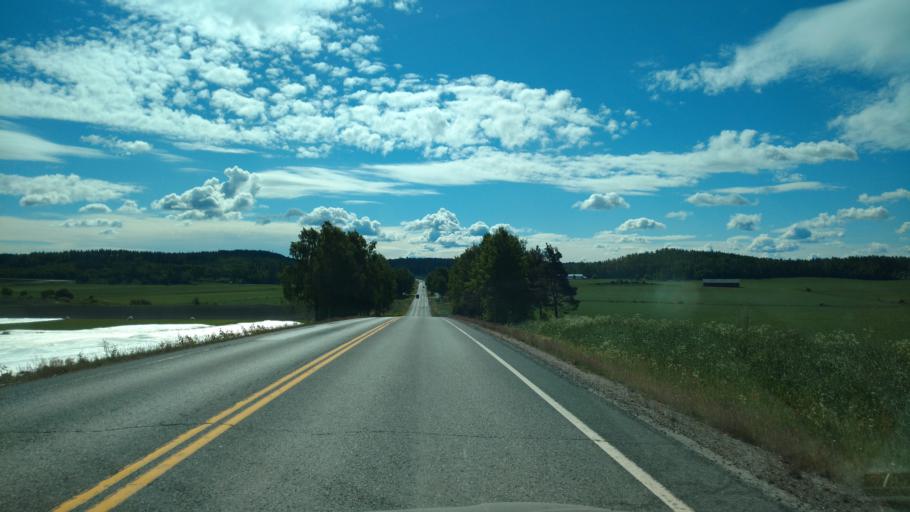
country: FI
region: Varsinais-Suomi
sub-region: Salo
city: Muurla
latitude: 60.3807
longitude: 23.2970
